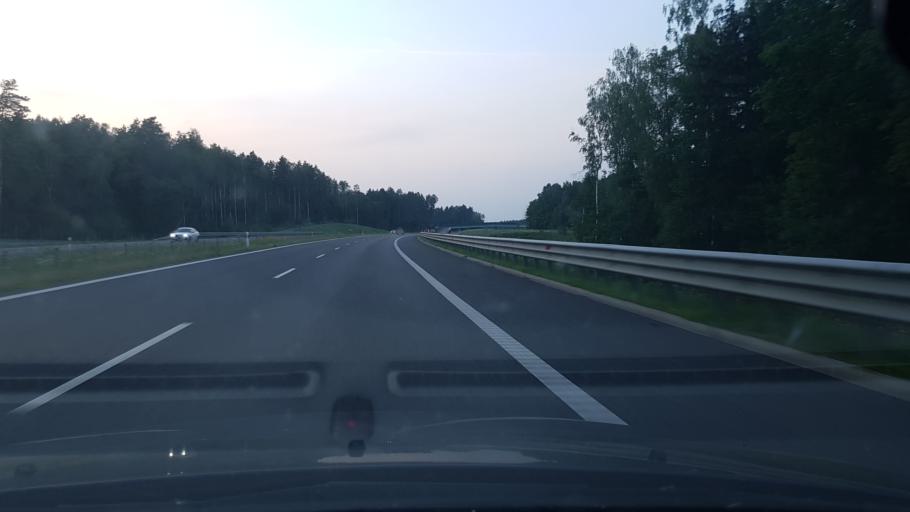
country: PL
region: Warmian-Masurian Voivodeship
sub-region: Powiat olsztynski
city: Olsztynek
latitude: 53.4549
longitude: 20.3220
